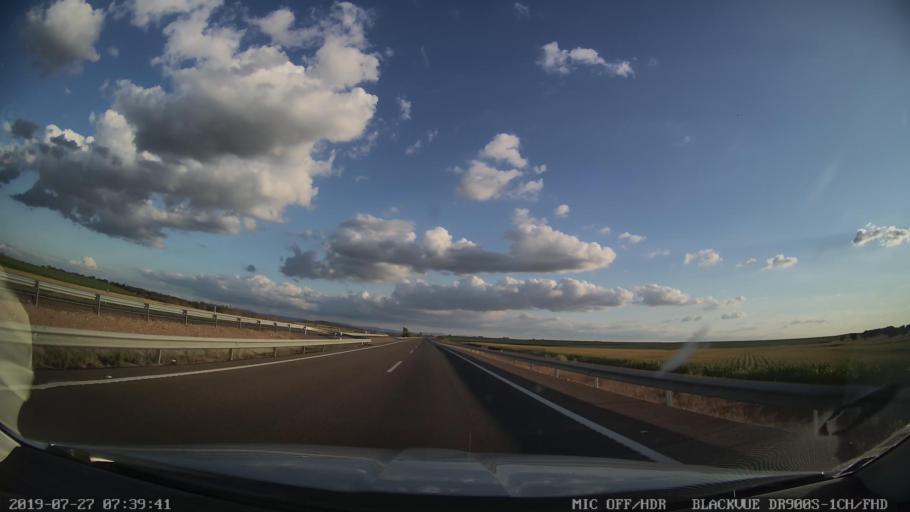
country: ES
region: Extremadura
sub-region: Provincia de Badajoz
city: Santa Amalia
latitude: 39.0600
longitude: -6.0561
